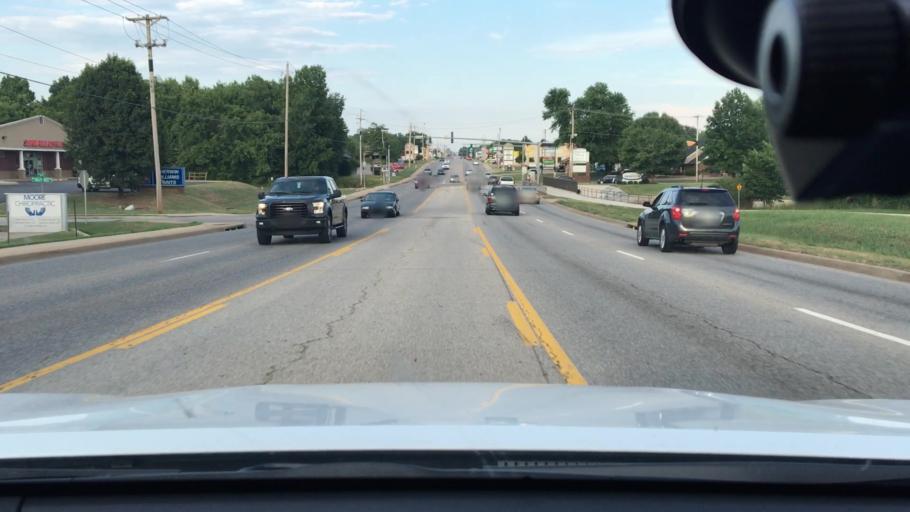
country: US
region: Arkansas
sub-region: Benton County
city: Rogers
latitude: 36.3345
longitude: -94.1631
